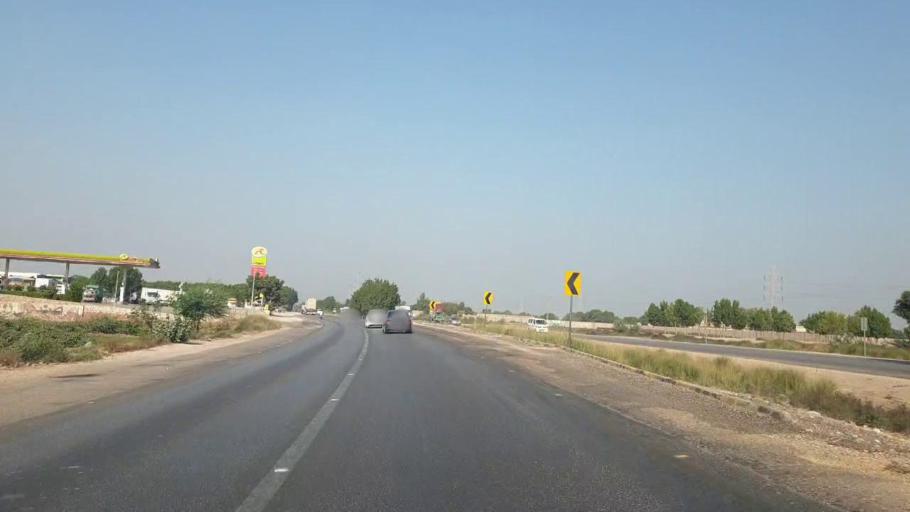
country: PK
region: Sindh
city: Matiari
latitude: 25.4906
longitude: 68.4219
